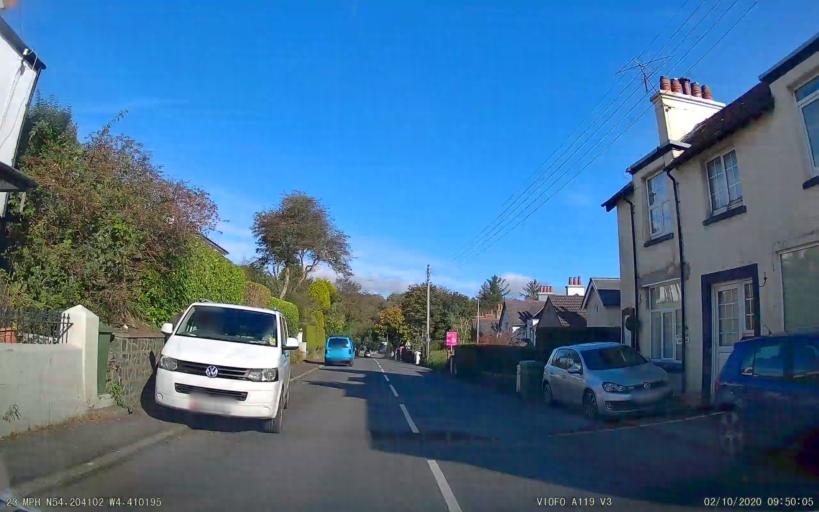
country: IM
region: Laxey
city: Laxey
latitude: 54.2041
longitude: -4.4102
